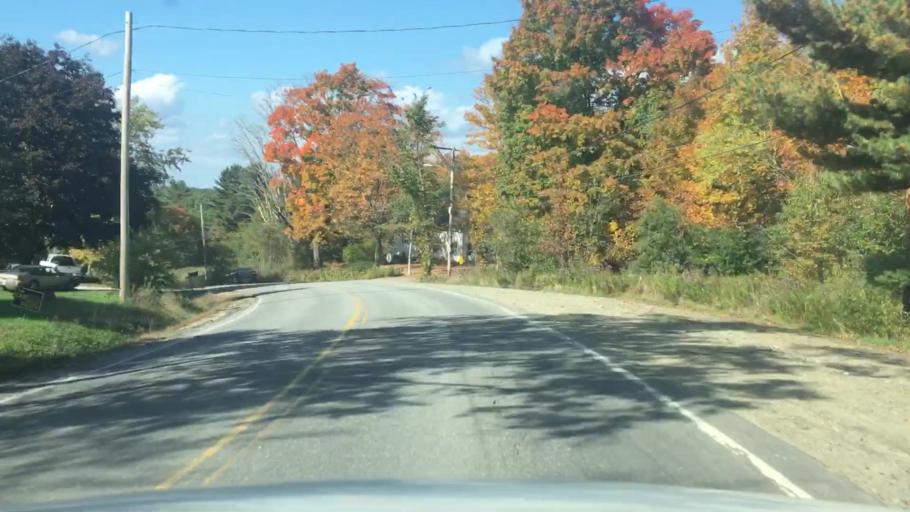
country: US
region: Maine
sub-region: Knox County
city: Thomaston
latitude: 44.0812
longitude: -69.2056
